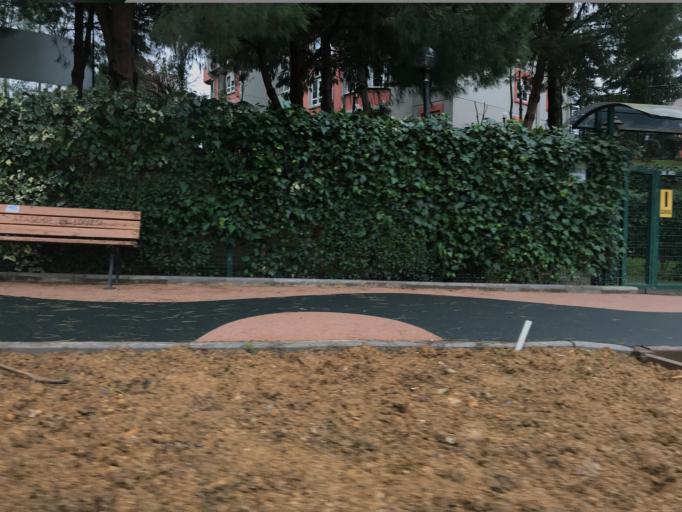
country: TR
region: Istanbul
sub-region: Atasehir
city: Atasehir
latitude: 40.9890
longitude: 29.1359
